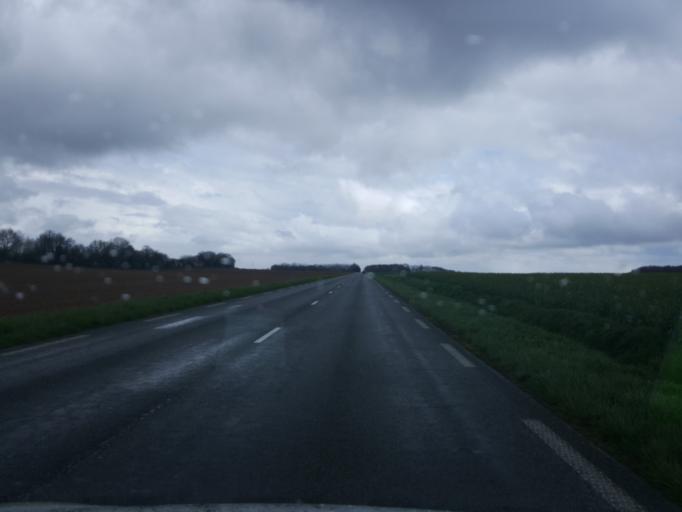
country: FR
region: Picardie
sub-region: Departement de l'Oise
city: Trie-Chateau
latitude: 49.2949
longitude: 1.8536
